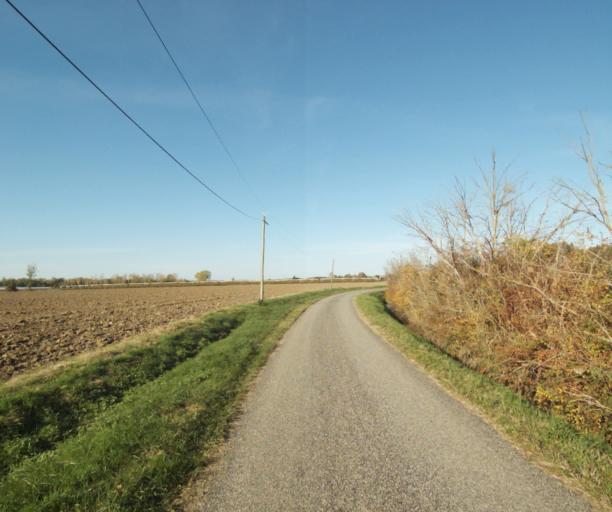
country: FR
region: Midi-Pyrenees
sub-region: Departement du Tarn-et-Garonne
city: Finhan
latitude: 43.9293
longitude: 1.2057
